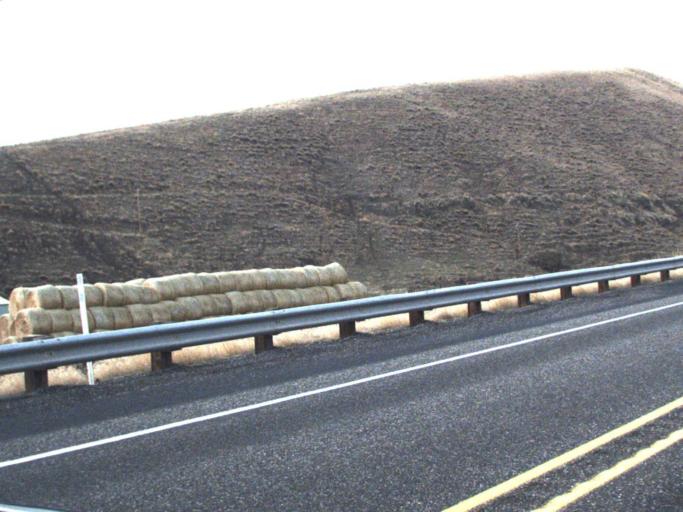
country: US
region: Washington
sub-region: Asotin County
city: Clarkston Heights-Vineland
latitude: 46.4321
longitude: -117.3170
